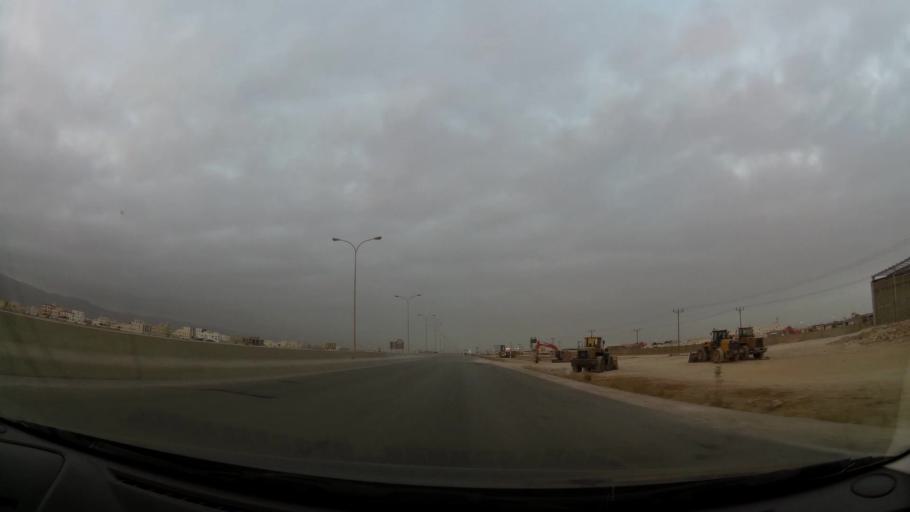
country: OM
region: Zufar
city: Salalah
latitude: 17.0323
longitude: 54.0314
